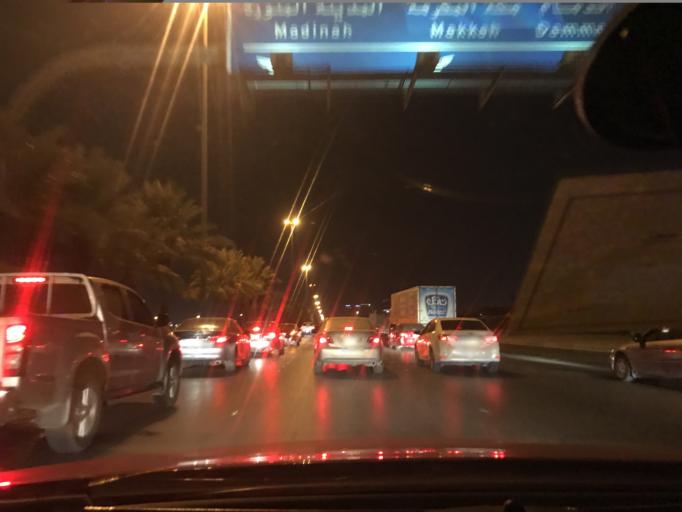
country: SA
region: Ar Riyad
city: Riyadh
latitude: 24.7681
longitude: 46.7348
